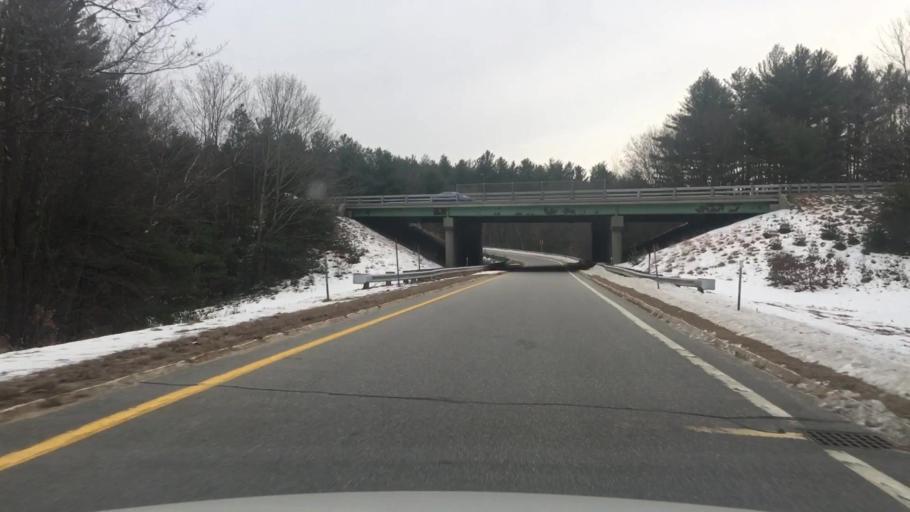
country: US
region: New Hampshire
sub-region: Merrimack County
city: Hopkinton
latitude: 43.1845
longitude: -71.6568
